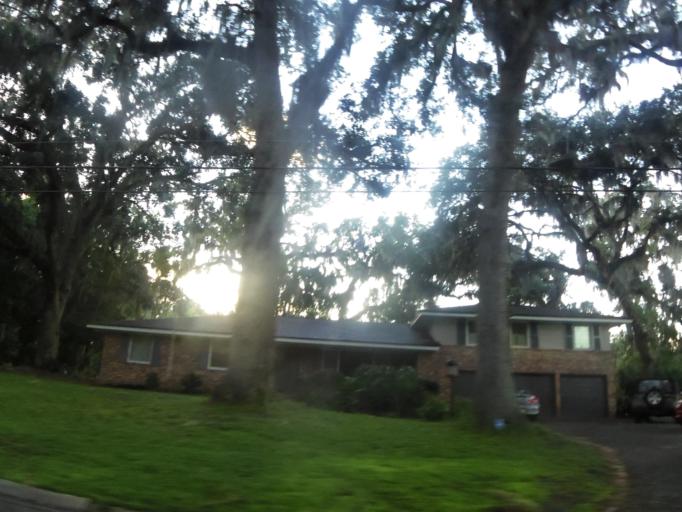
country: US
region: Florida
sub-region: Duval County
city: Jacksonville
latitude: 30.2368
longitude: -81.6251
